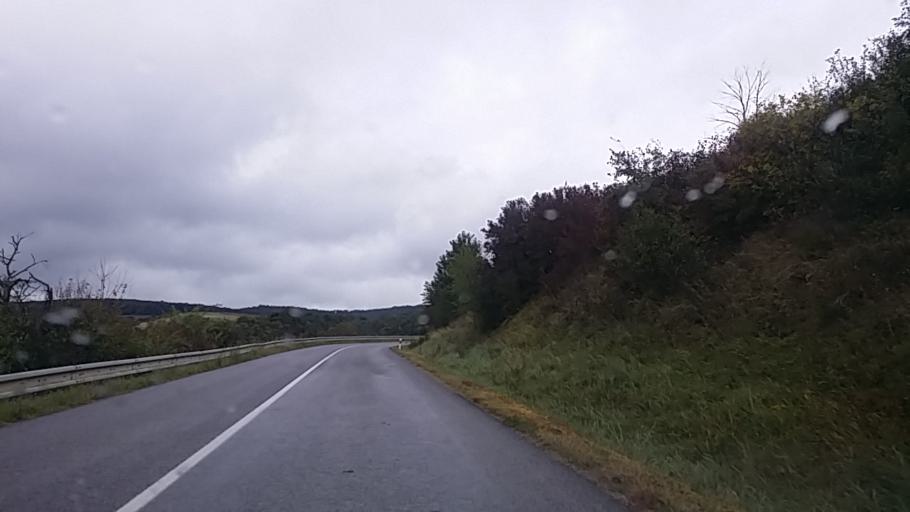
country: HU
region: Komarom-Esztergom
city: Esztergom
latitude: 47.8613
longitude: 18.7425
